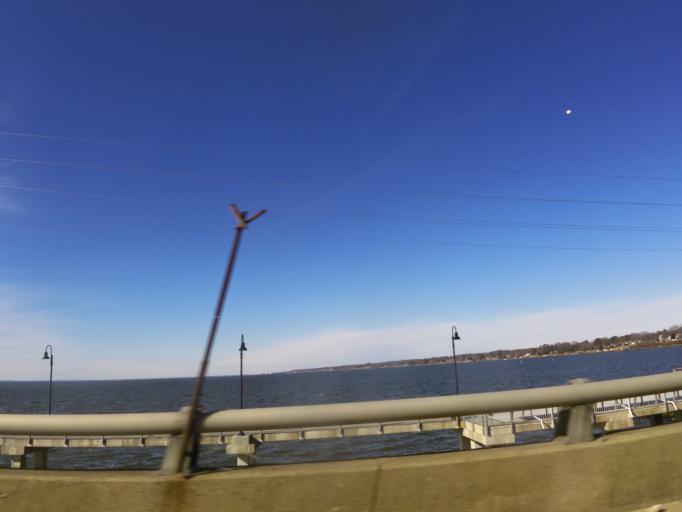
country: US
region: Virginia
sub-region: City of Newport News
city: Newport News
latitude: 37.0132
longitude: -76.4562
